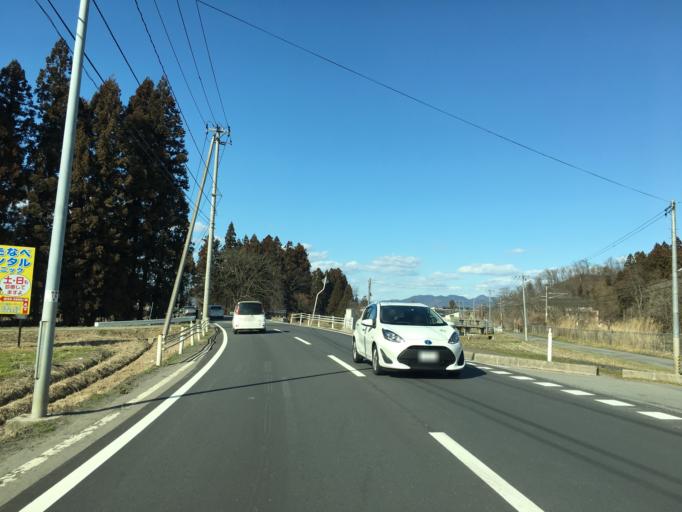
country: JP
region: Yamagata
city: Yonezawa
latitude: 37.9475
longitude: 140.1387
